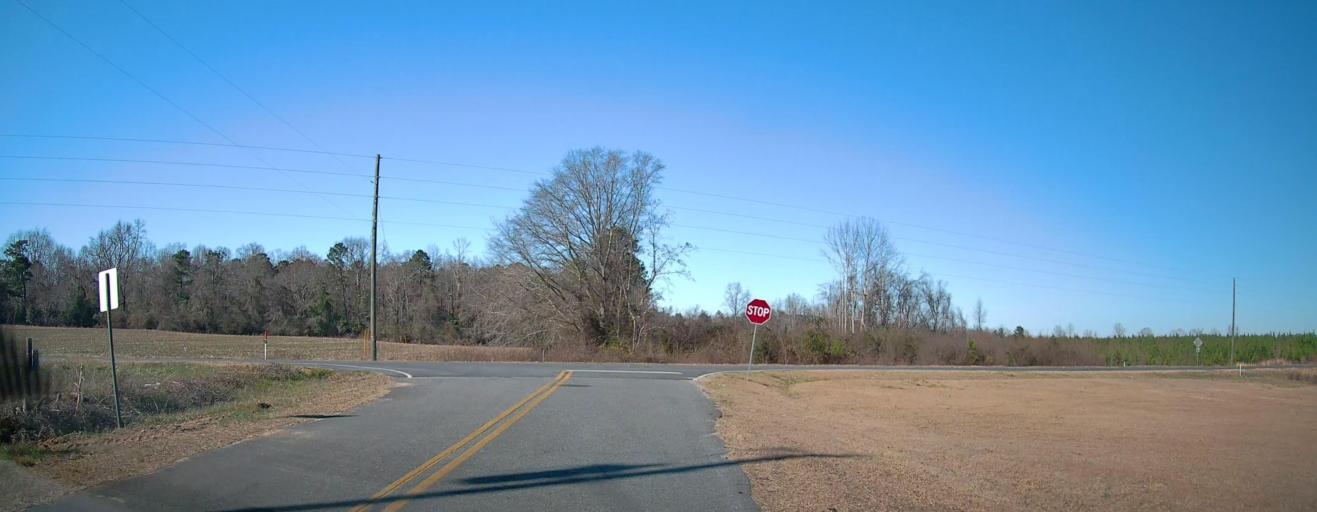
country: US
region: Georgia
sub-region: Taylor County
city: Butler
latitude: 32.6585
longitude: -84.3251
